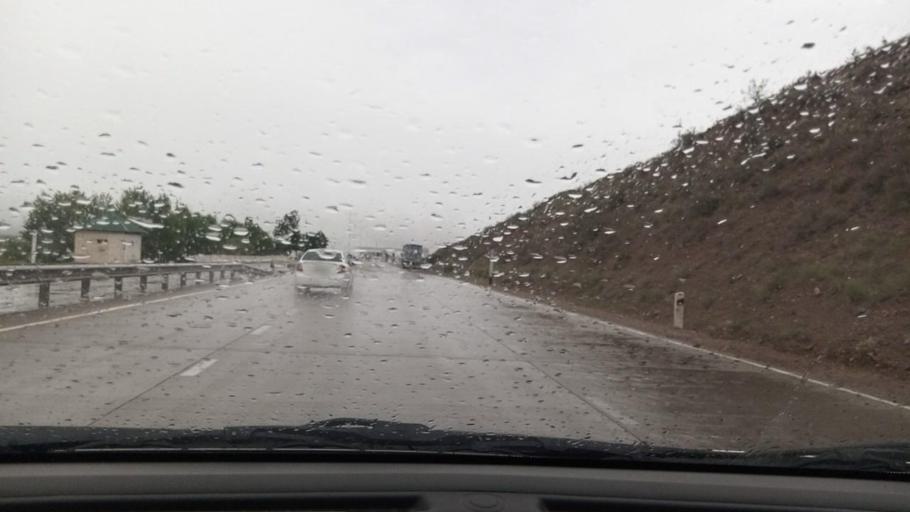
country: UZ
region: Namangan
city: Pop Shahri
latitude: 40.9239
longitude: 70.7292
